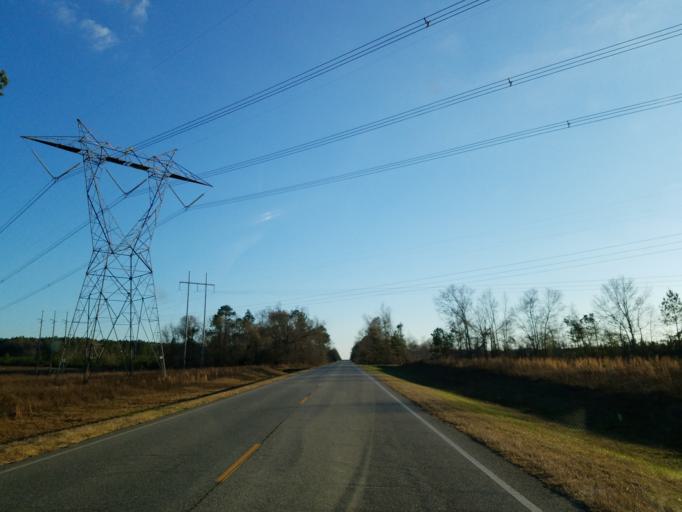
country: US
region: Georgia
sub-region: Turner County
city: Ashburn
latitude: 31.7115
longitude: -83.8081
